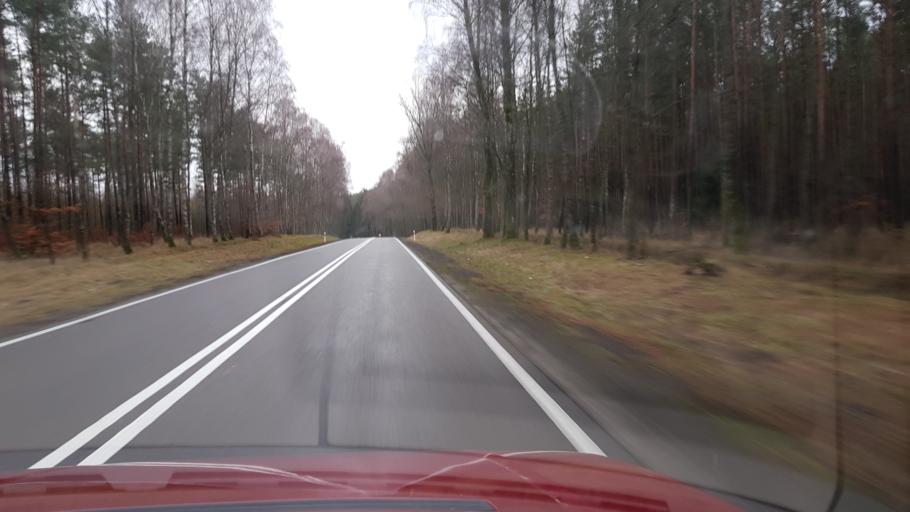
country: PL
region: West Pomeranian Voivodeship
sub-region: Powiat drawski
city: Drawsko Pomorskie
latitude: 53.4931
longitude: 15.7056
